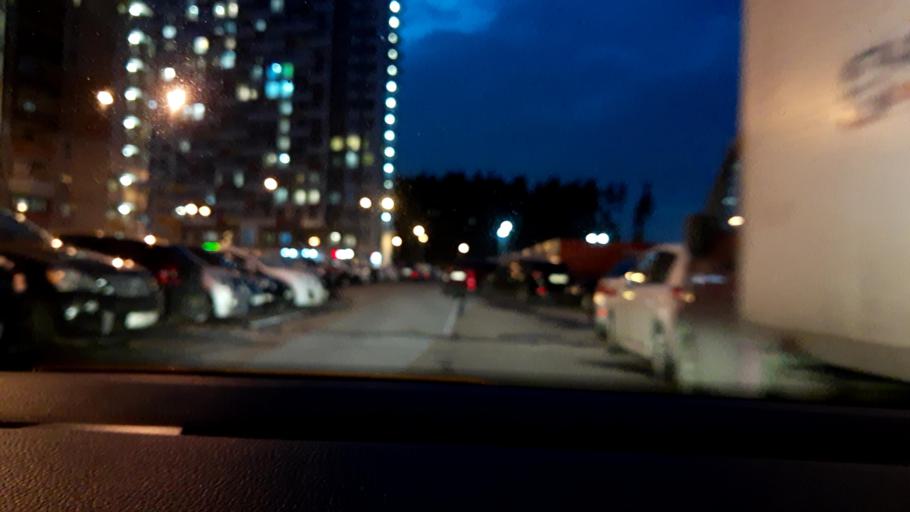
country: RU
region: Moscow
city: Vostochnyy
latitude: 55.8247
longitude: 37.8904
